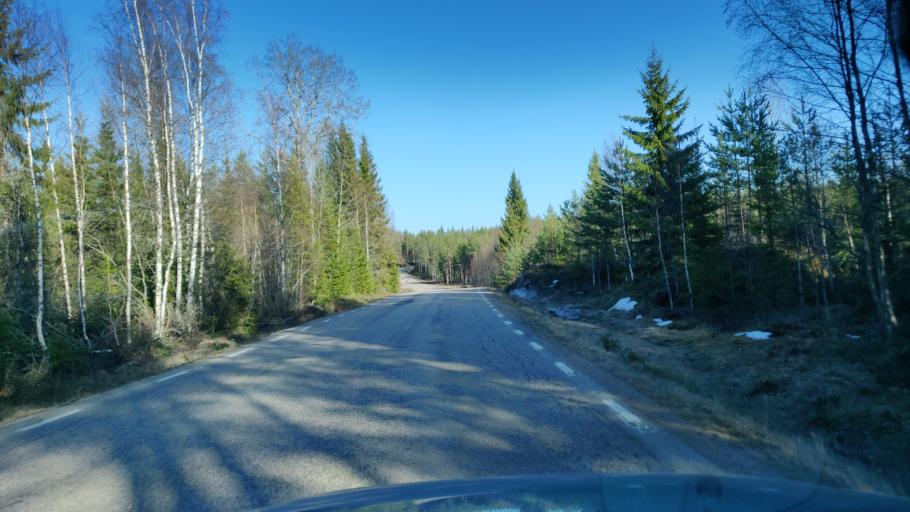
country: SE
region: Vaermland
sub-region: Hagfors Kommun
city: Ekshaerad
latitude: 59.9848
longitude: 13.3474
